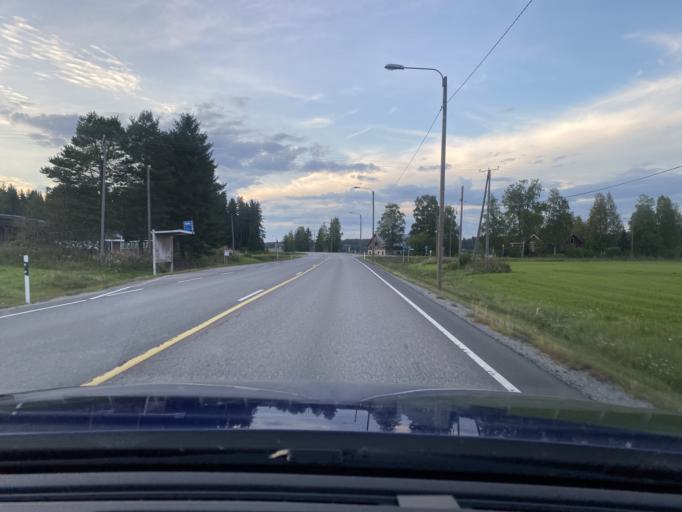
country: FI
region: Satakunta
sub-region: Pohjois-Satakunta
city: Kankaanpaeae
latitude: 61.7419
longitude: 22.5249
